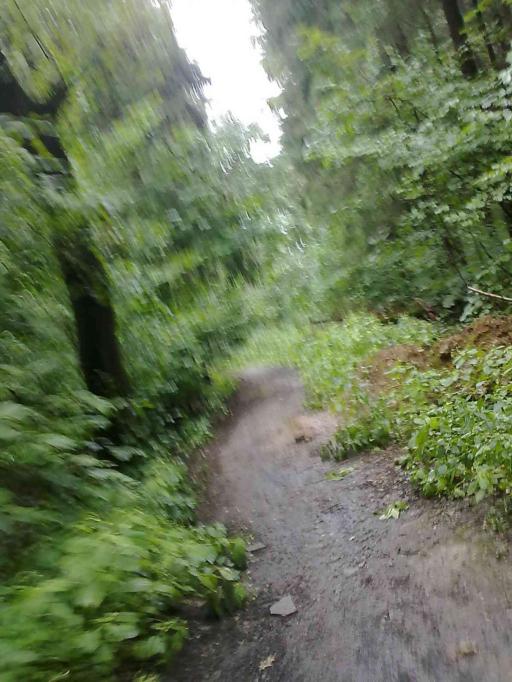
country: RU
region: Moskovskaya
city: Odintsovo
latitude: 55.6404
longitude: 37.2585
